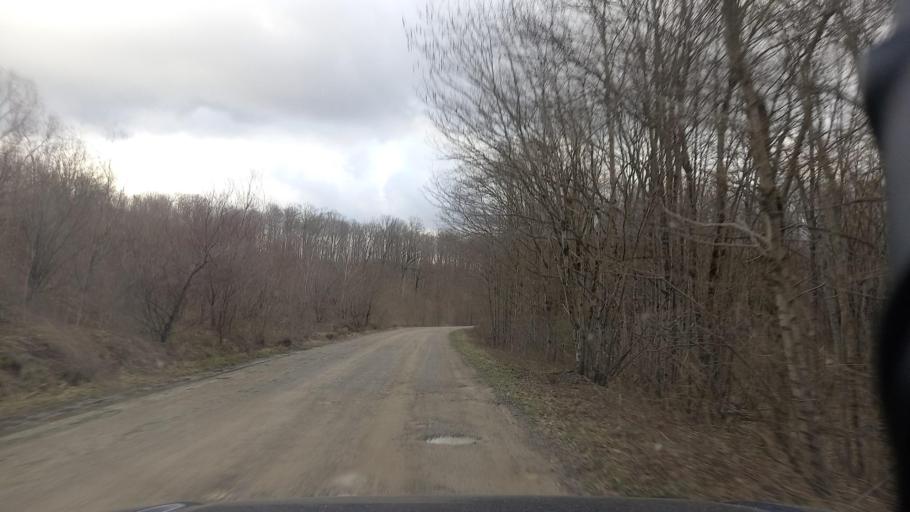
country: RU
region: Krasnodarskiy
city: Lermontovo
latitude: 44.4808
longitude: 38.7967
